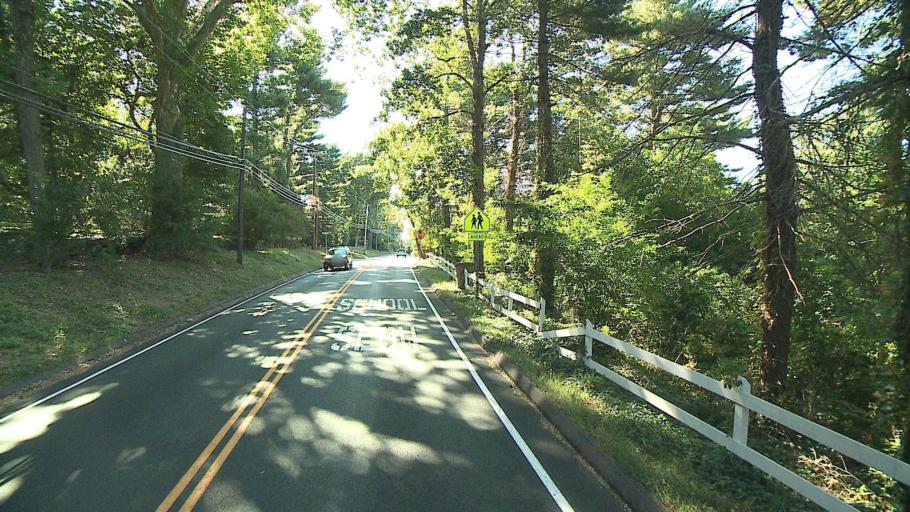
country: US
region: Connecticut
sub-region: Fairfield County
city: Darien
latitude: 41.1055
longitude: -73.4840
